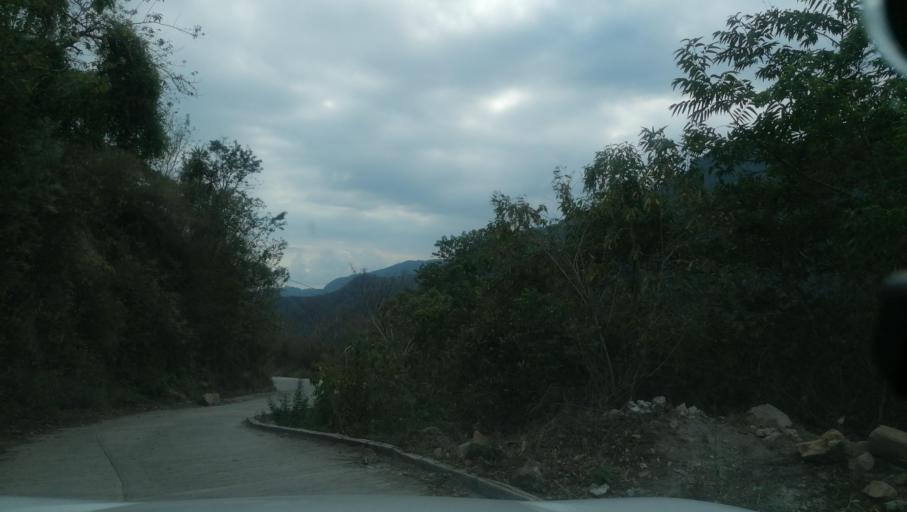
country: MX
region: Chiapas
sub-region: Cacahoatan
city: Benito Juarez
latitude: 15.1648
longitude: -92.1754
